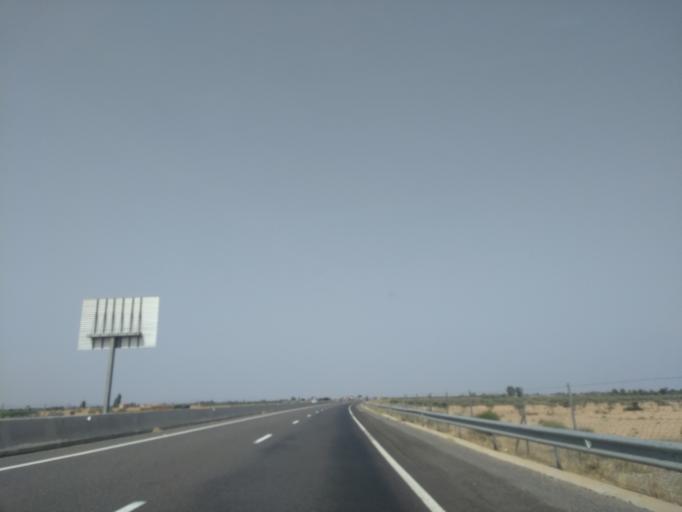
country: MA
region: Marrakech-Tensift-Al Haouz
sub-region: Marrakech
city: Marrakesh
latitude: 31.6126
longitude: -8.3839
